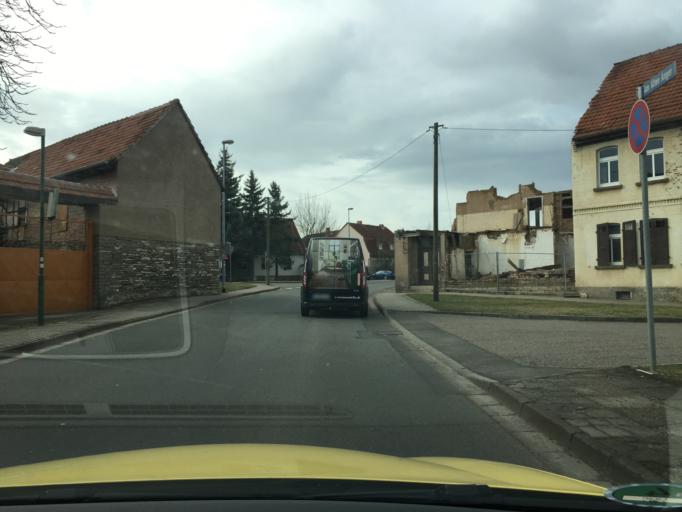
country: DE
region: Thuringia
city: Kleinmolsen
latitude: 51.0169
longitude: 11.1158
